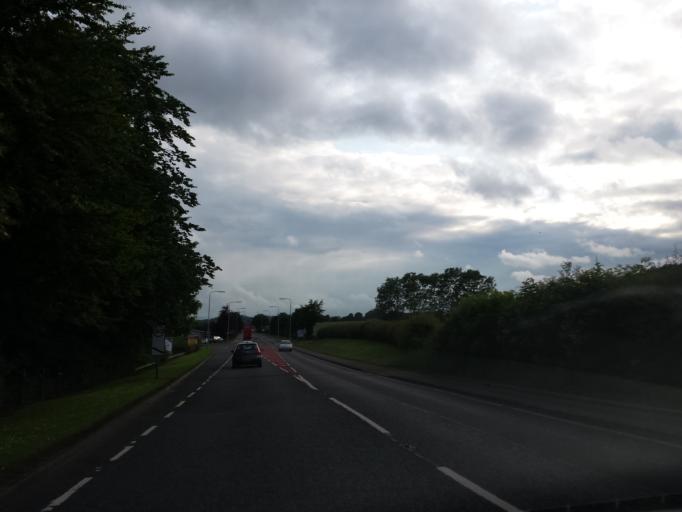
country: GB
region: Scotland
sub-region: Fife
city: Cupar
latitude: 56.3264
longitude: -2.9862
